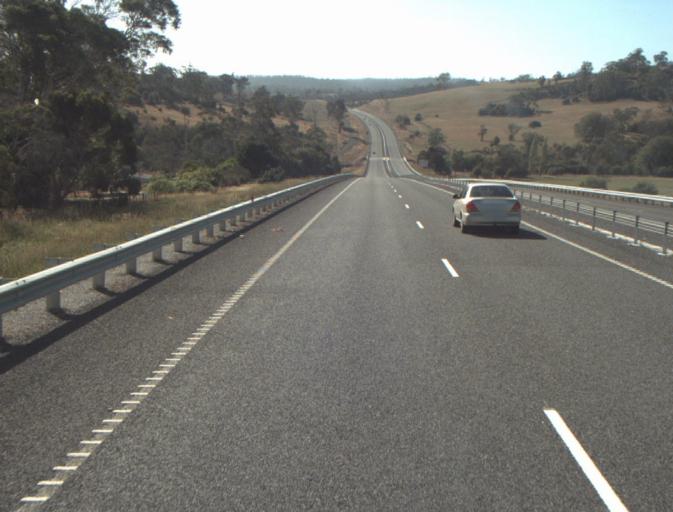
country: AU
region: Tasmania
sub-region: Launceston
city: Mayfield
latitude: -41.3669
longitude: 147.1086
